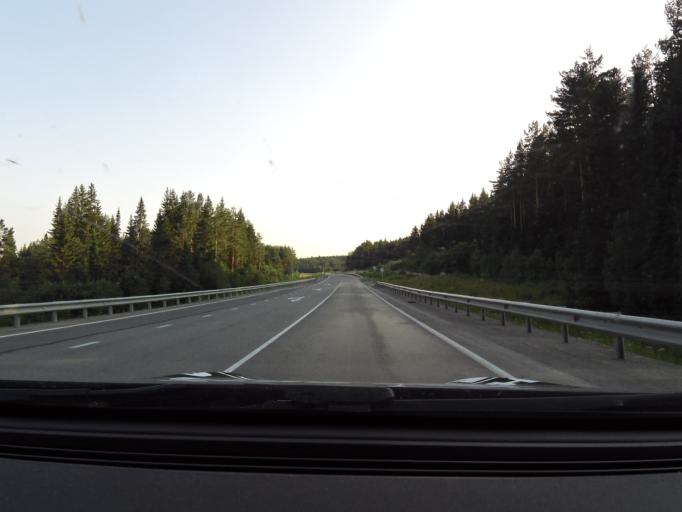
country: RU
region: Sverdlovsk
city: Nizhniye Sergi
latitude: 56.6510
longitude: 59.2545
